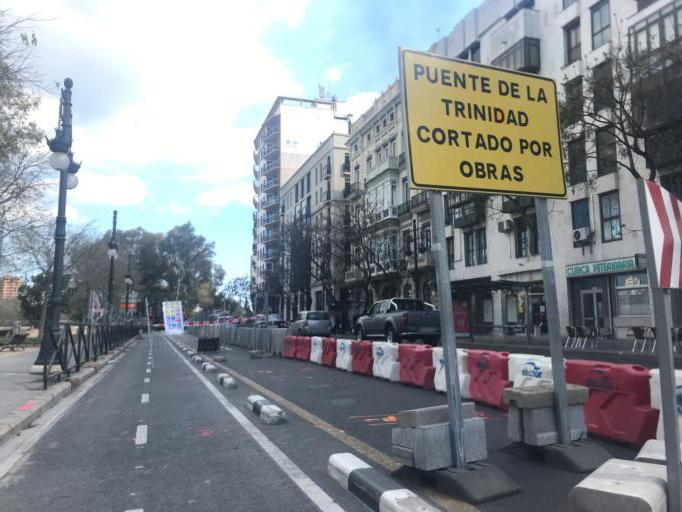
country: ES
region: Valencia
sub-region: Provincia de Valencia
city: Valencia
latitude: 39.4789
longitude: -0.3744
